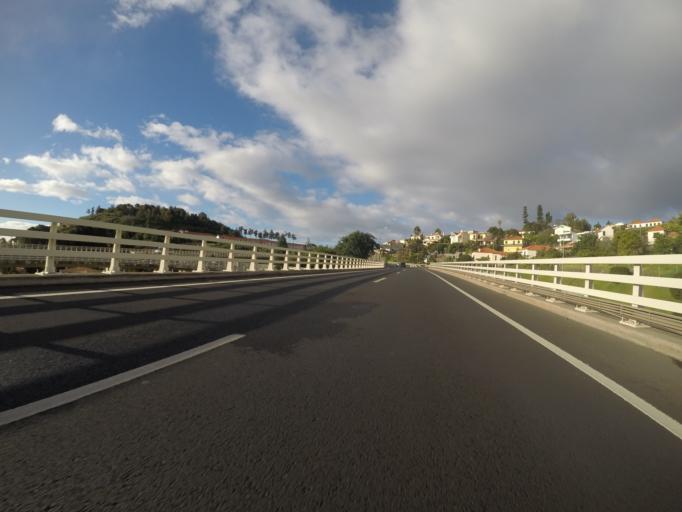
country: PT
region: Madeira
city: Camara de Lobos
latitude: 32.6552
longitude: -16.9374
